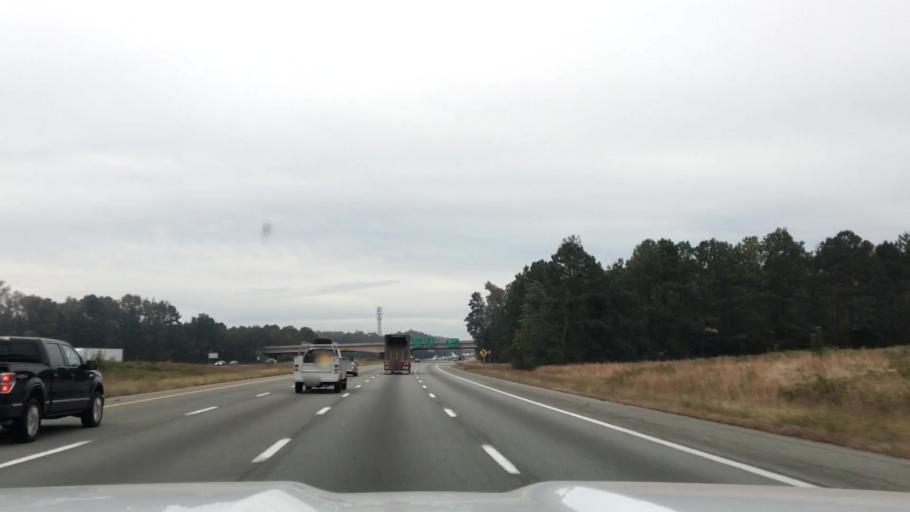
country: US
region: Virginia
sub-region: Henrico County
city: Highland Springs
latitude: 37.5525
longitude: -77.2884
